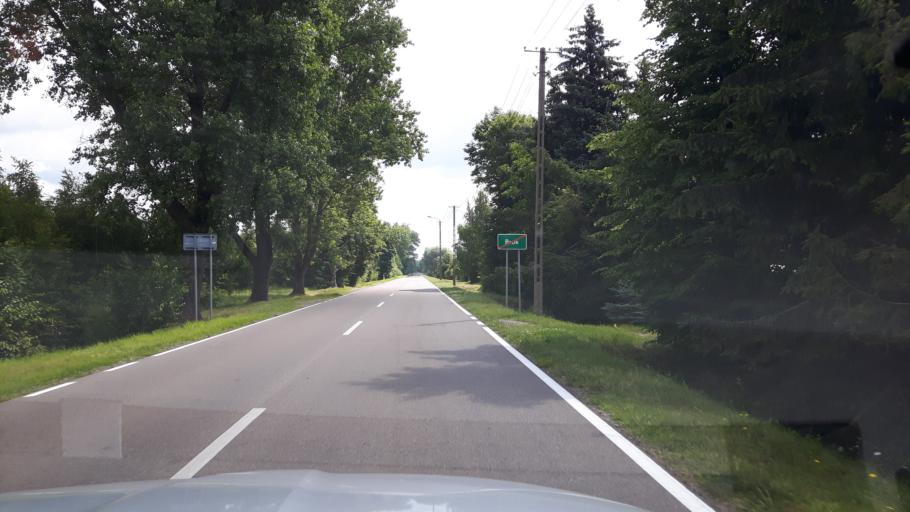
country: PL
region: Masovian Voivodeship
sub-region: Powiat ostrowski
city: Brok
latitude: 52.7040
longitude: 21.8951
